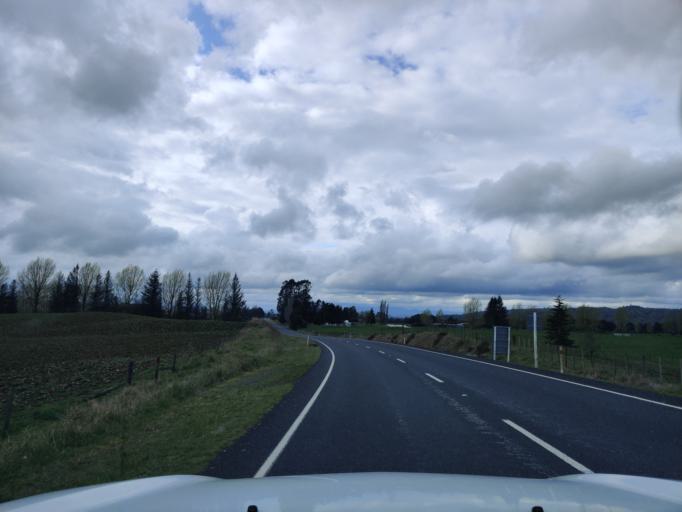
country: NZ
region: Waikato
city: Turangi
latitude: -39.0502
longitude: 175.3835
